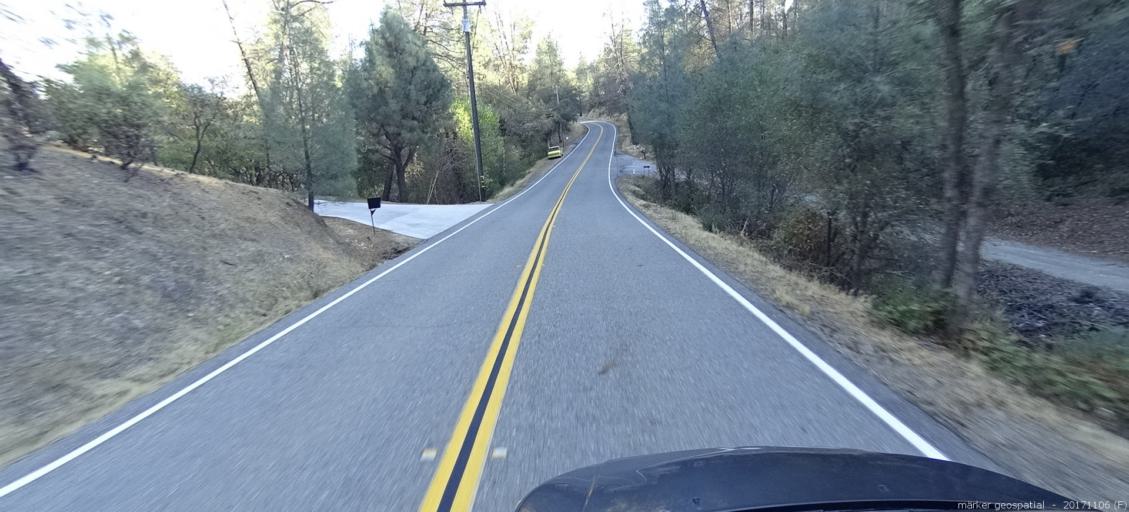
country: US
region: California
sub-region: Shasta County
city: Shasta
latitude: 40.5710
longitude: -122.4742
